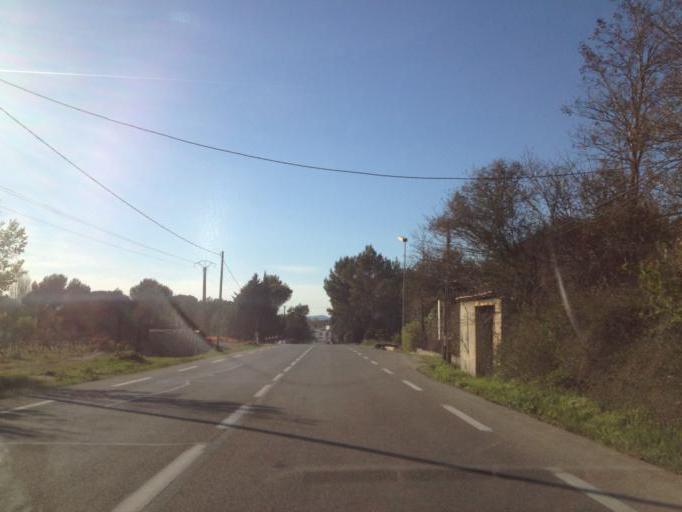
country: FR
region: Provence-Alpes-Cote d'Azur
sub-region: Departement des Bouches-du-Rhone
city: Saint-Cannat
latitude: 43.6092
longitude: 5.3301
